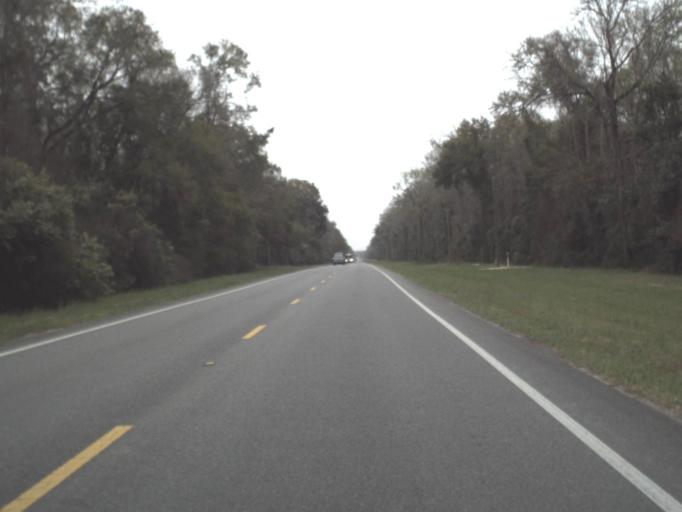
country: US
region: Florida
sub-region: Wakulla County
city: Crawfordville
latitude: 30.1482
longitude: -84.2867
